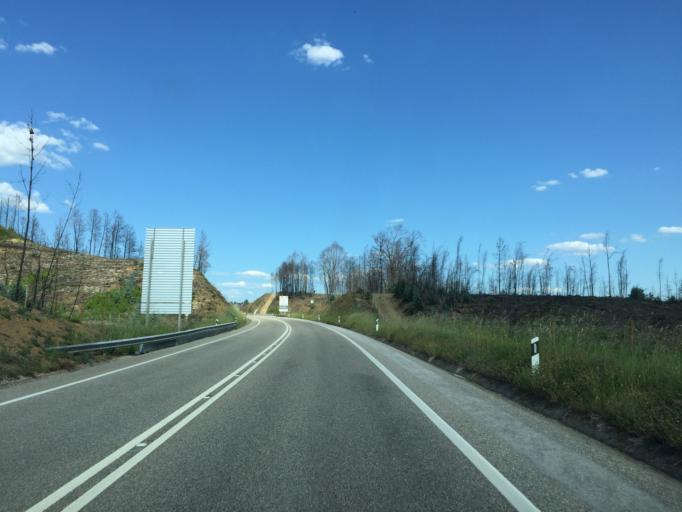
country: PT
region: Leiria
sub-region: Pedrogao Grande
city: Pedrogao Grande
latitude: 39.9259
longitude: -8.1728
